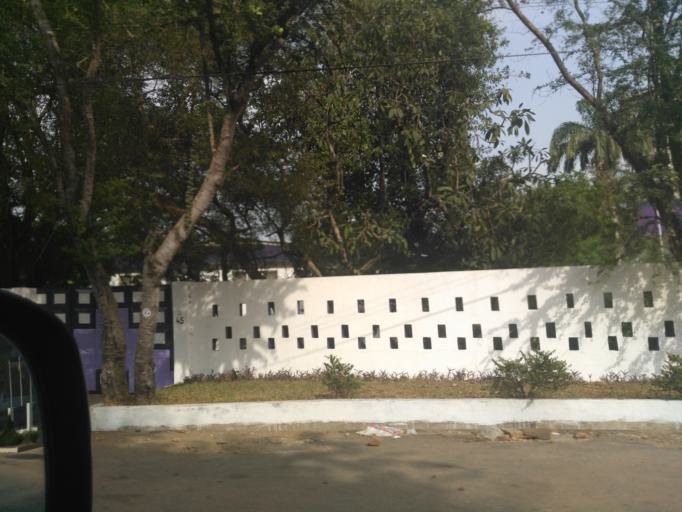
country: GH
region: Greater Accra
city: Accra
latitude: 5.6095
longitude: -0.1837
